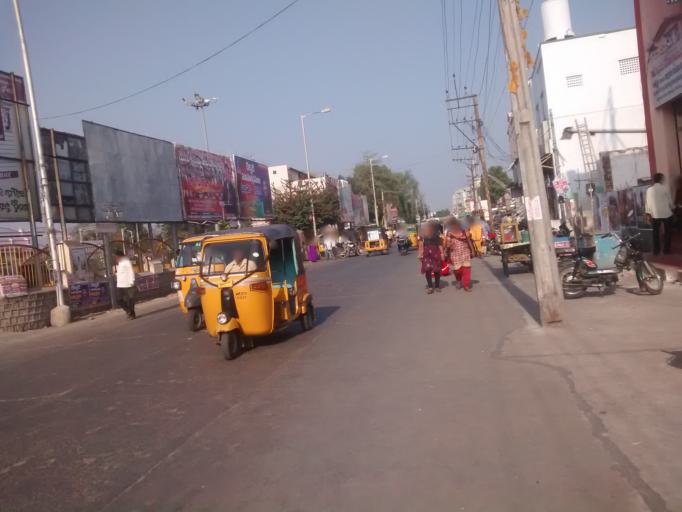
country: IN
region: Andhra Pradesh
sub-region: Prakasam
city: Chirala
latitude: 15.8304
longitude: 80.3542
